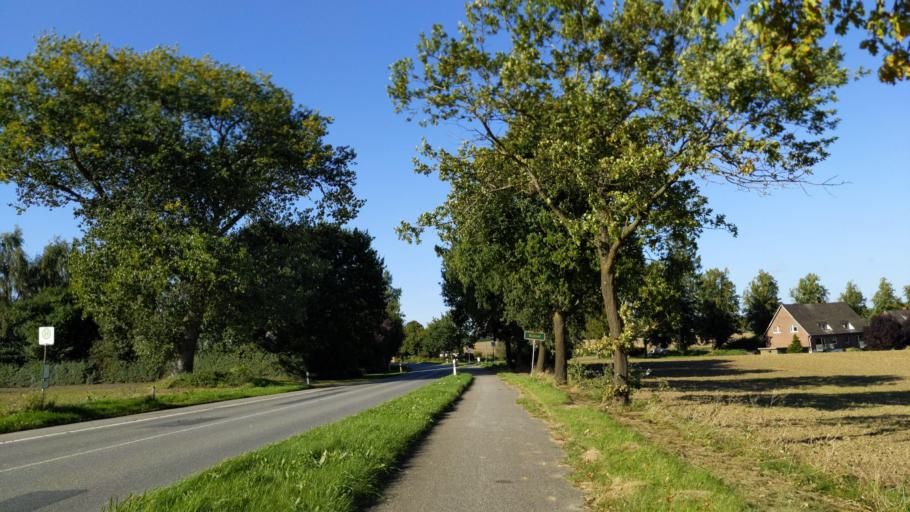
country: DE
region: Schleswig-Holstein
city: Ahrensbok
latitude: 53.9668
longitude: 10.6016
